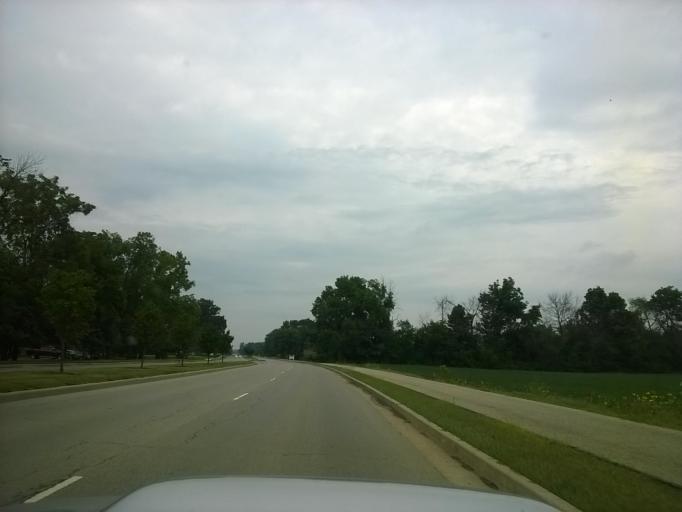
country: US
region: Indiana
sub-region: Hamilton County
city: Carmel
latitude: 39.9515
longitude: -86.1553
